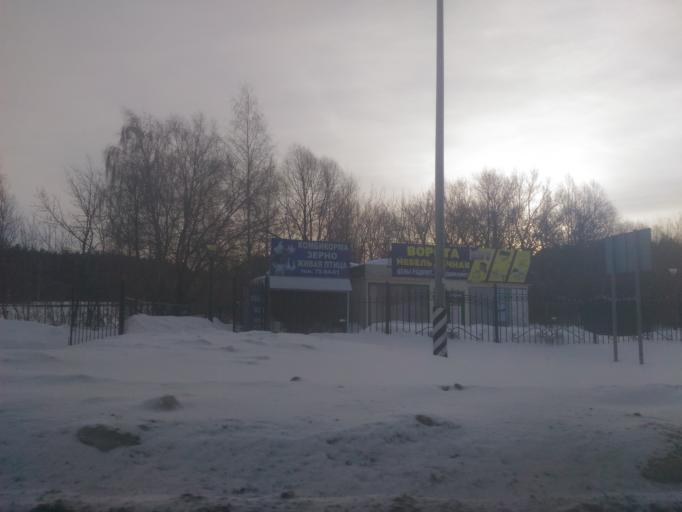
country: RU
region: Ulyanovsk
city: Isheyevka
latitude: 54.3746
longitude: 48.3089
